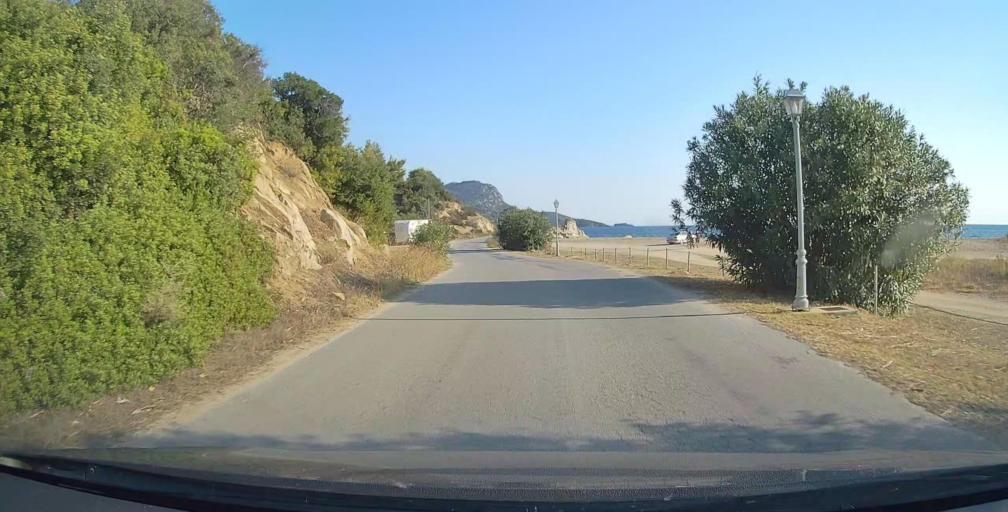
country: GR
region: Central Macedonia
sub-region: Nomos Chalkidikis
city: Sykia
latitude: 39.9918
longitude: 23.8933
